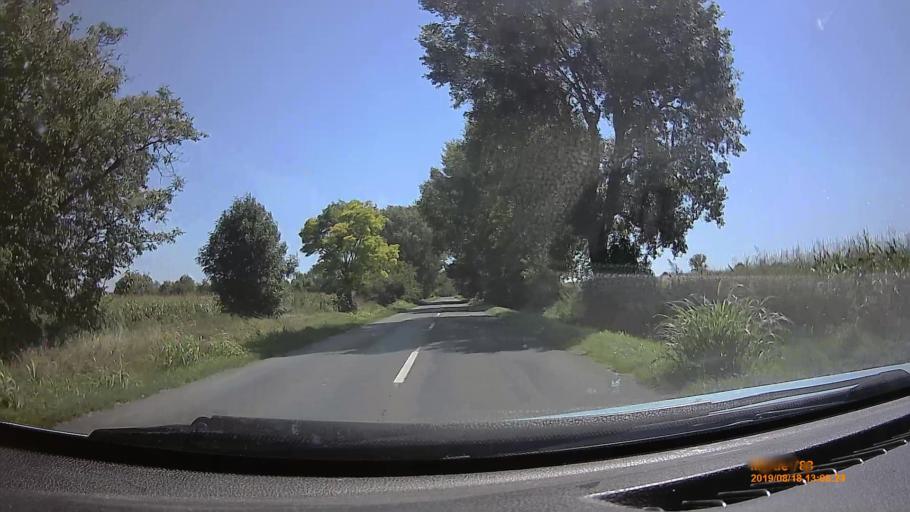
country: HU
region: Fejer
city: Kaloz
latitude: 46.9393
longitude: 18.5022
